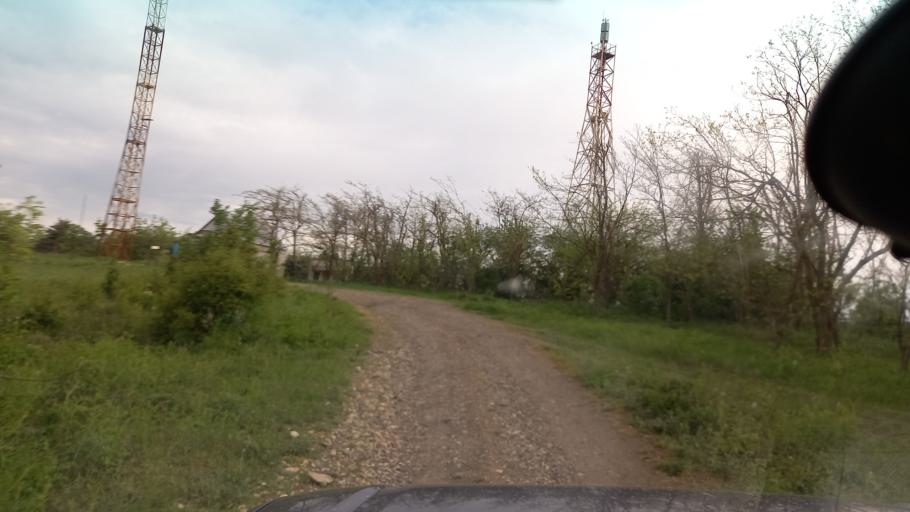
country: RU
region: Kabardino-Balkariya
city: Kuba-Taba
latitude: 43.8142
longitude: 43.4097
